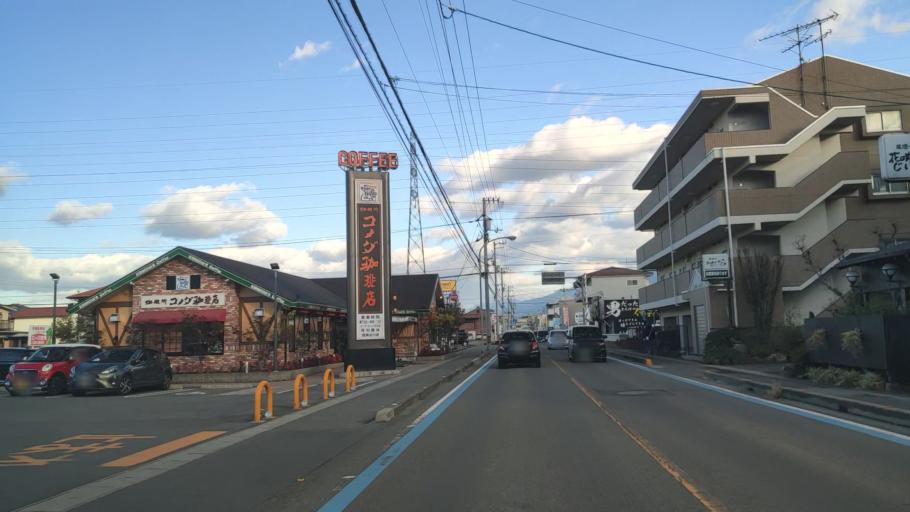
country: JP
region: Ehime
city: Saijo
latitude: 33.9152
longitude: 133.1678
